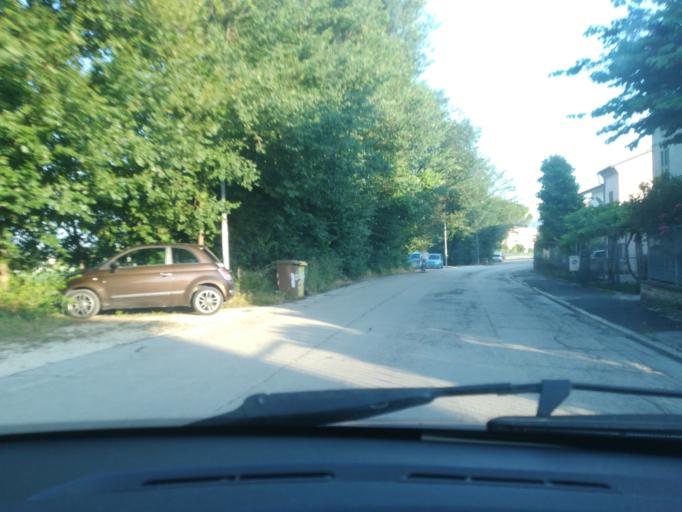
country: IT
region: The Marches
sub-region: Provincia di Macerata
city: Piediripa
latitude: 43.2816
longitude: 13.4821
